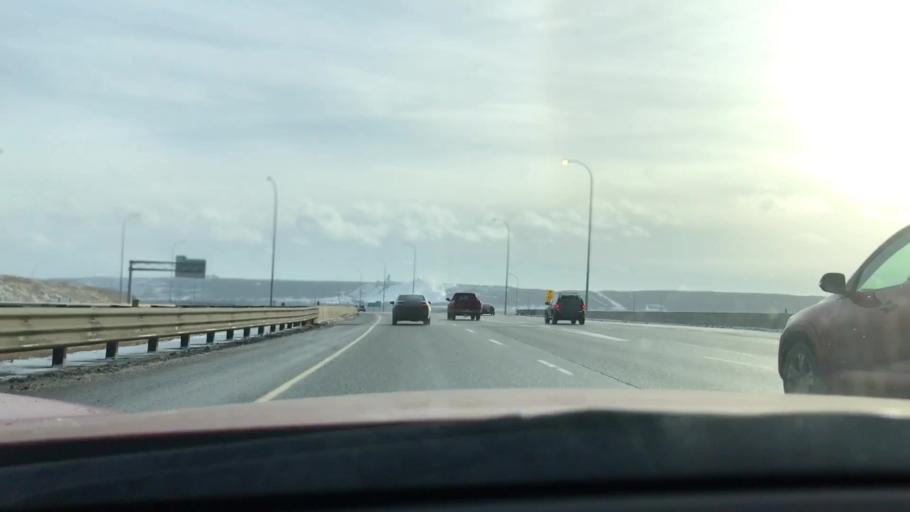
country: CA
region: Alberta
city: Calgary
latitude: 51.1192
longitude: -114.2312
